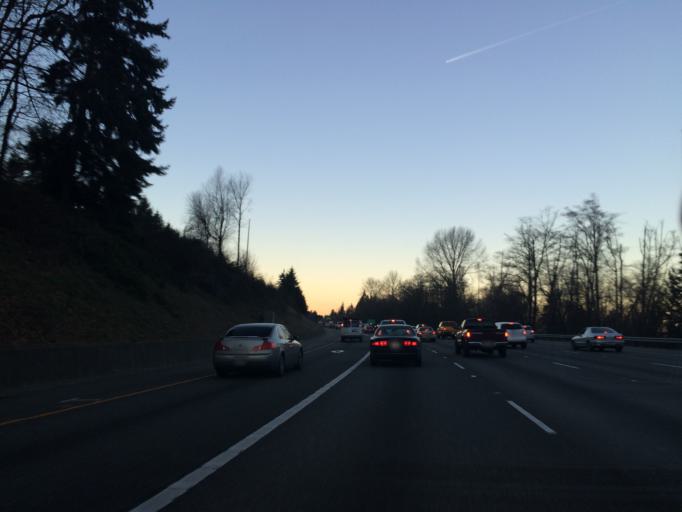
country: US
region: Washington
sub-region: Snohomish County
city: Everett
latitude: 47.9419
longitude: -122.1966
